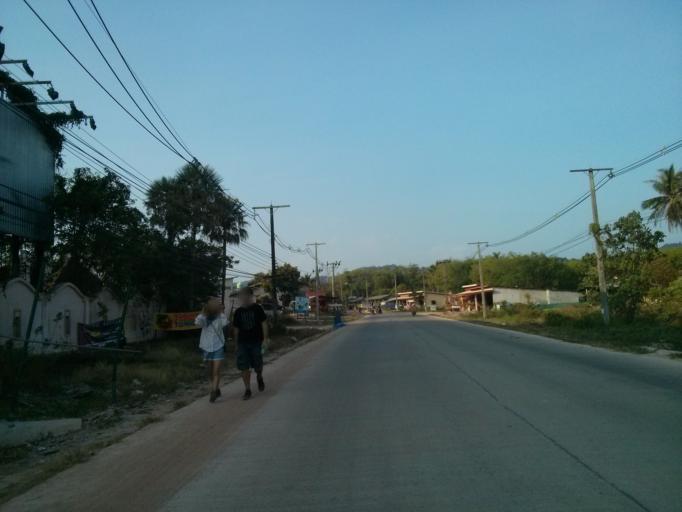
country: TH
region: Krabi
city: Saladan
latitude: 7.5827
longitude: 99.0336
